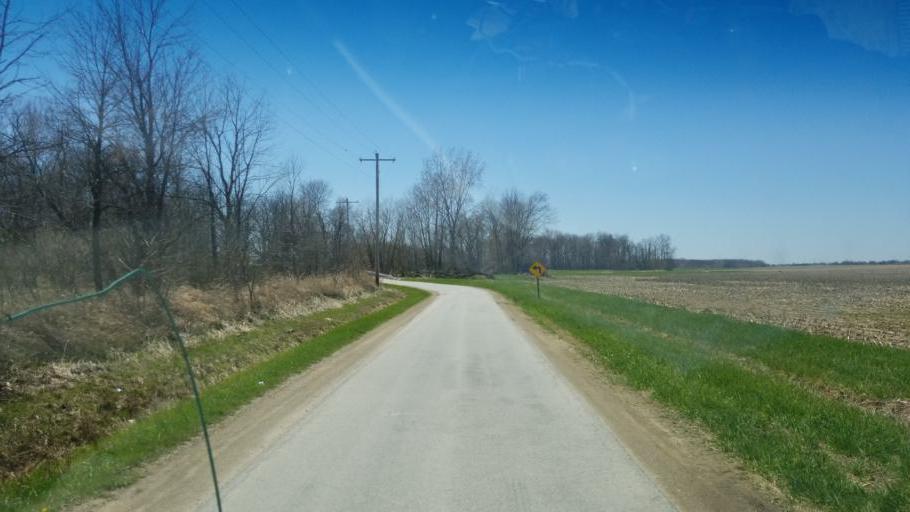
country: US
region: Ohio
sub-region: Huron County
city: Willard
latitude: 41.0449
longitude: -82.8493
